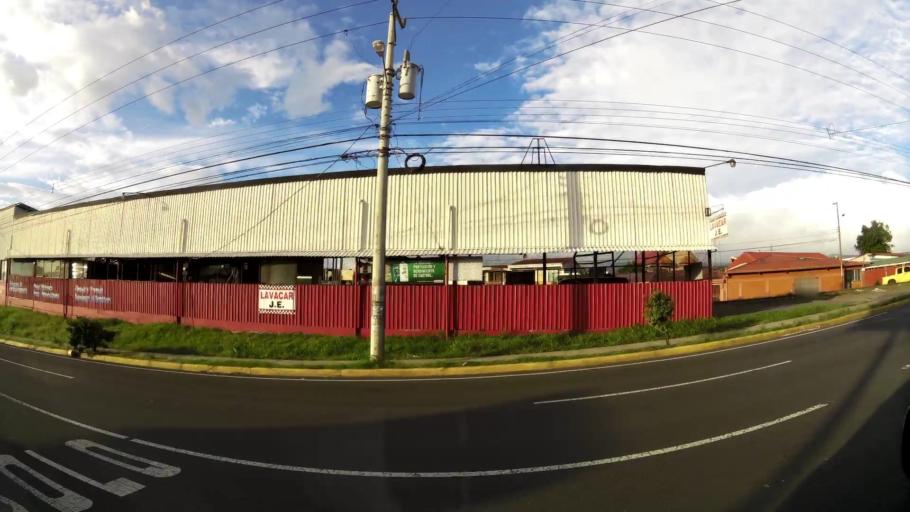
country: CR
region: Heredia
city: San Francisco
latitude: 9.9963
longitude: -84.1330
